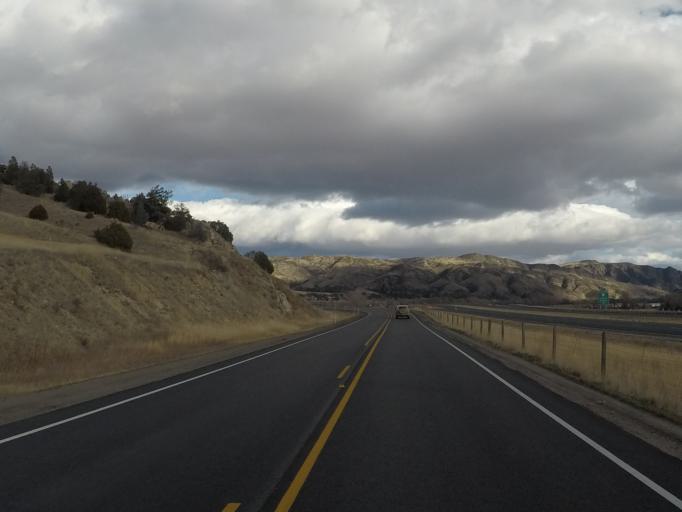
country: US
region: Montana
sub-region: Jefferson County
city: Whitehall
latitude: 45.8713
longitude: -111.9624
